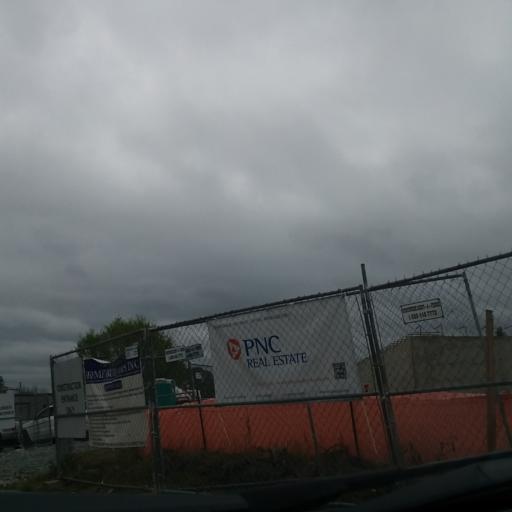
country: US
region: Washington
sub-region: King County
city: Boulevard Park
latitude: 47.4983
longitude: -122.3081
